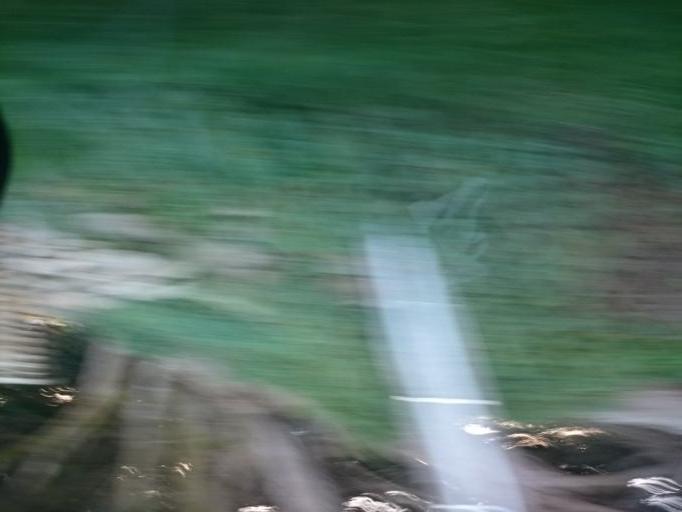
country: FR
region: Brittany
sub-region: Departement du Finistere
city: Landunvez
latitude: 48.5316
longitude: -4.7494
